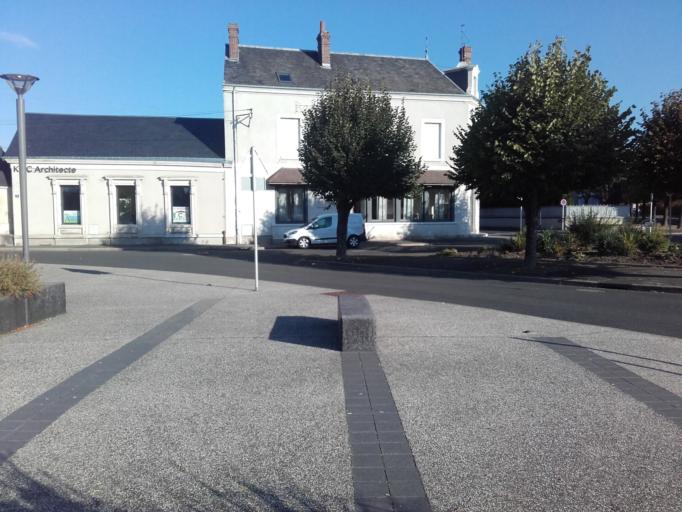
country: FR
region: Centre
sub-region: Departement du Loir-et-Cher
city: Vendome
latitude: 47.8028
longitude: 1.0702
